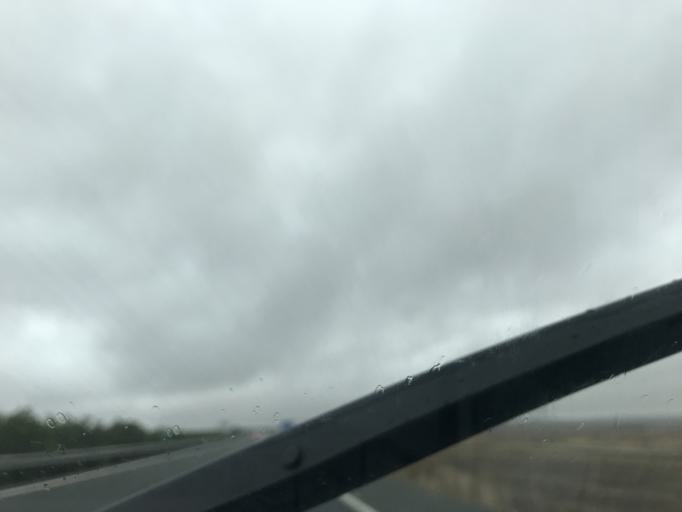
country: ES
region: Andalusia
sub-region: Provincia de Malaga
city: Fuente de Piedra
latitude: 37.1448
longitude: -4.7346
